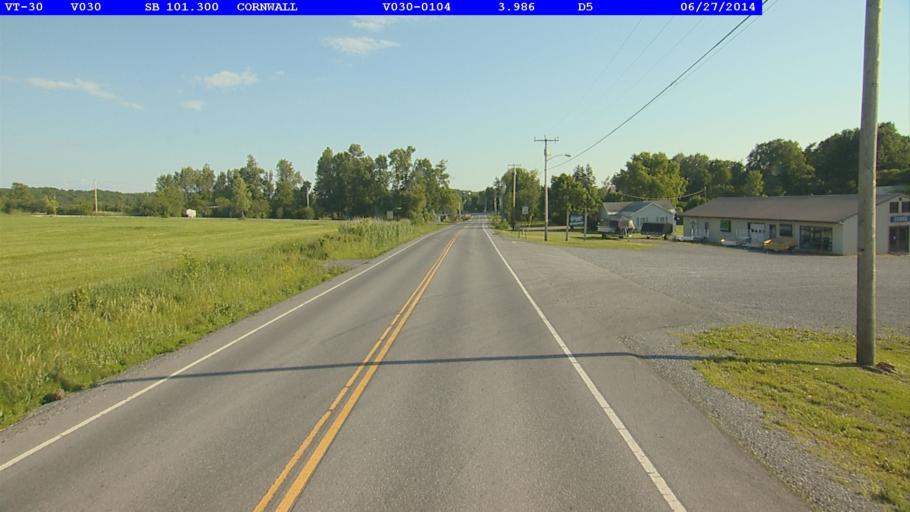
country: US
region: Vermont
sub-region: Addison County
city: Middlebury (village)
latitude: 43.9650
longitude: -73.2081
